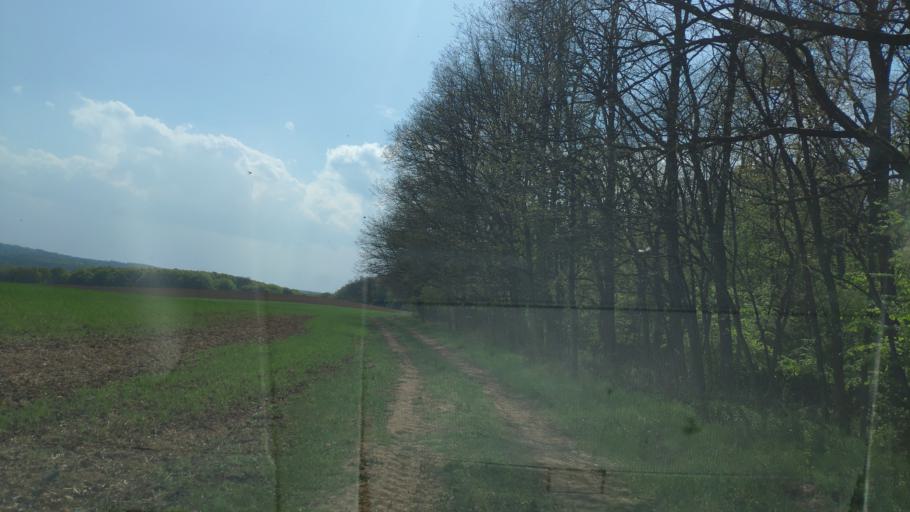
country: SK
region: Kosicky
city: Moldava nad Bodvou
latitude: 48.5465
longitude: 20.9467
